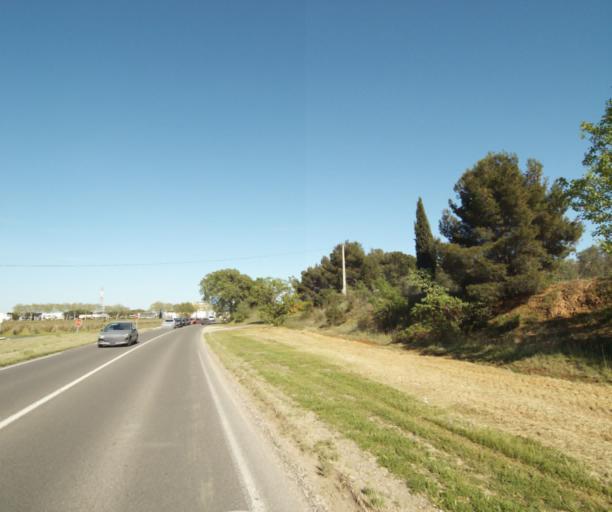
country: FR
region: Languedoc-Roussillon
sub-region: Departement de l'Herault
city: Lattes
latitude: 43.5764
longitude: 3.9278
